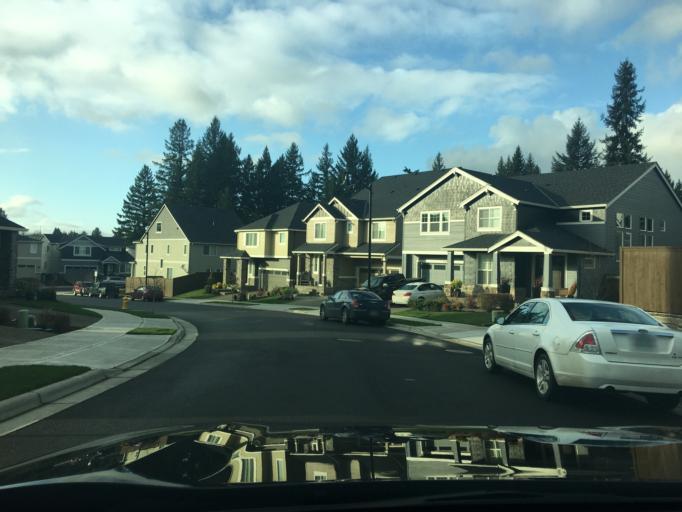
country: US
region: Oregon
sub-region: Washington County
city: Bethany
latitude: 45.5770
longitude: -122.8557
